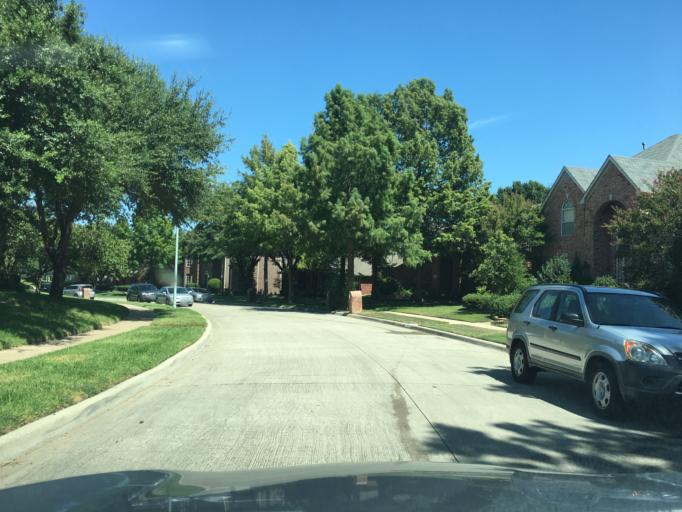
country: US
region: Texas
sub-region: Dallas County
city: Sachse
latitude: 32.9671
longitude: -96.6343
